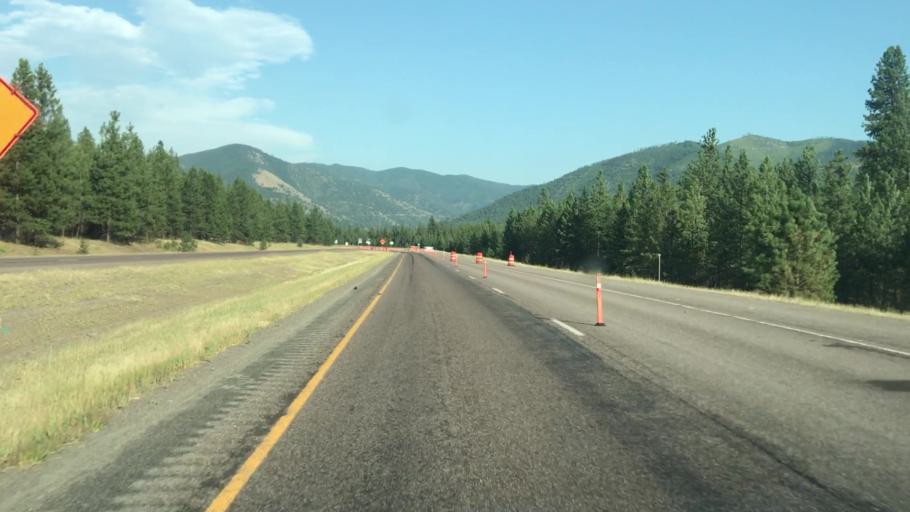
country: US
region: Montana
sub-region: Mineral County
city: Superior
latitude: 47.0145
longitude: -114.7316
